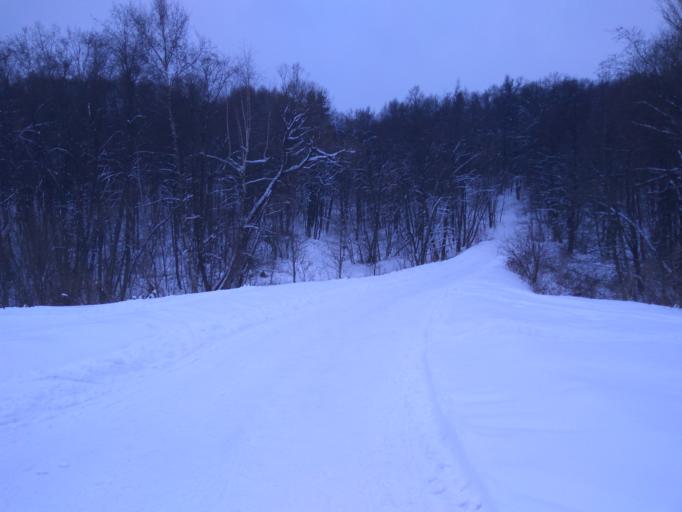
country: RU
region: Moscow
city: Orekhovo-Borisovo Severnoye
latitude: 55.6081
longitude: 37.6879
